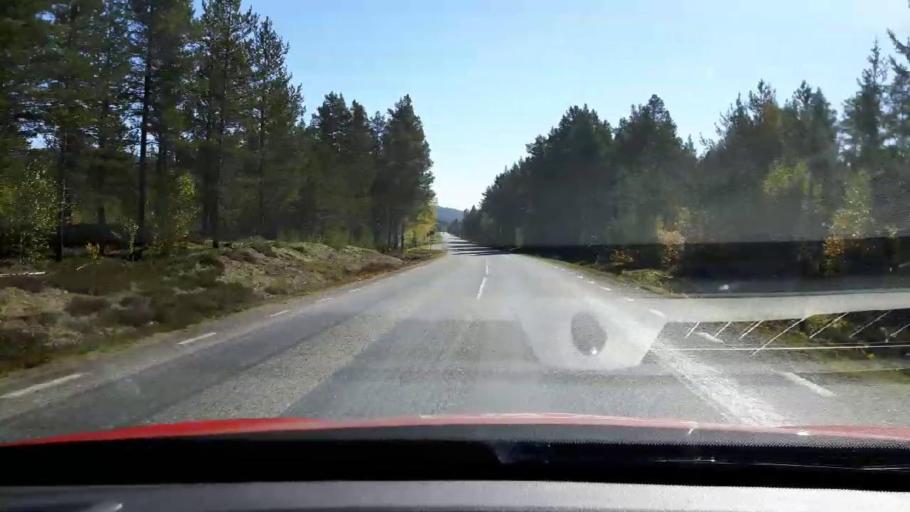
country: SE
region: Jaemtland
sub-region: Harjedalens Kommun
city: Sveg
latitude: 62.3583
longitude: 14.0099
